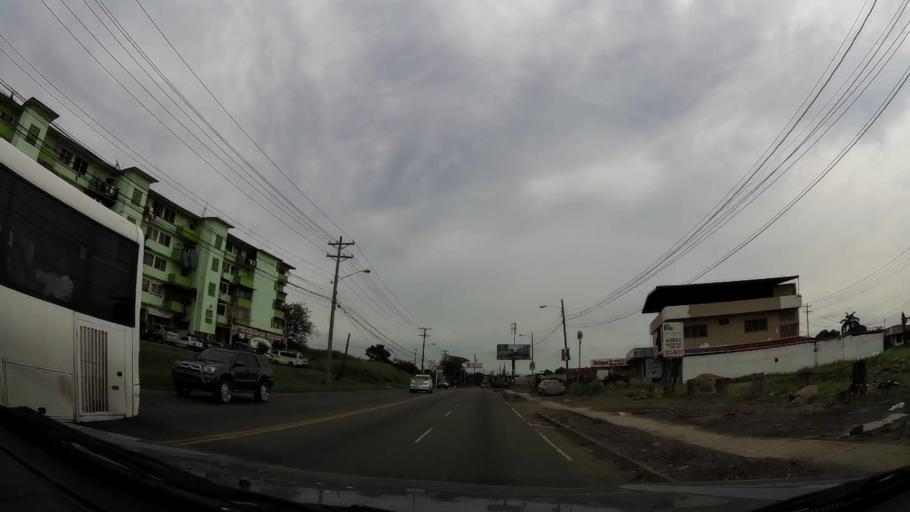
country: PA
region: Panama
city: San Miguelito
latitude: 9.0426
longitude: -79.4564
